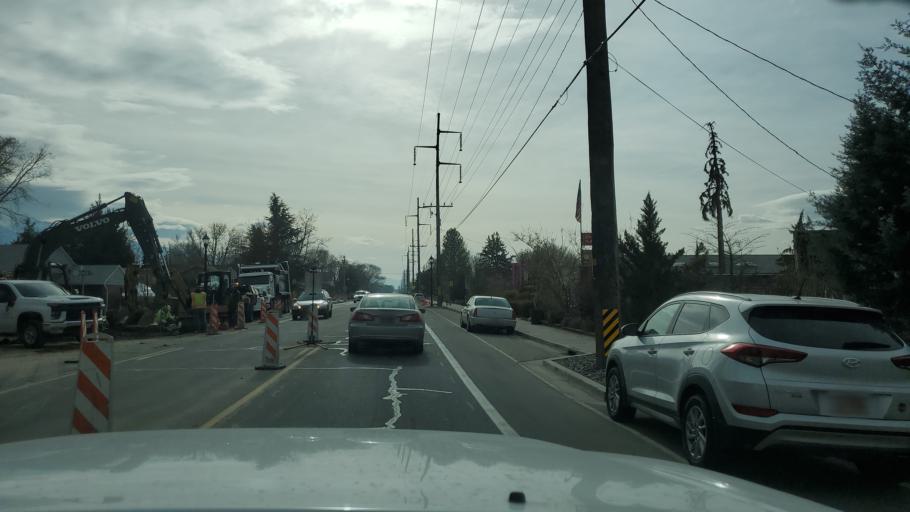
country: US
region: Utah
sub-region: Salt Lake County
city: Millcreek
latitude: 40.6957
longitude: -111.8655
